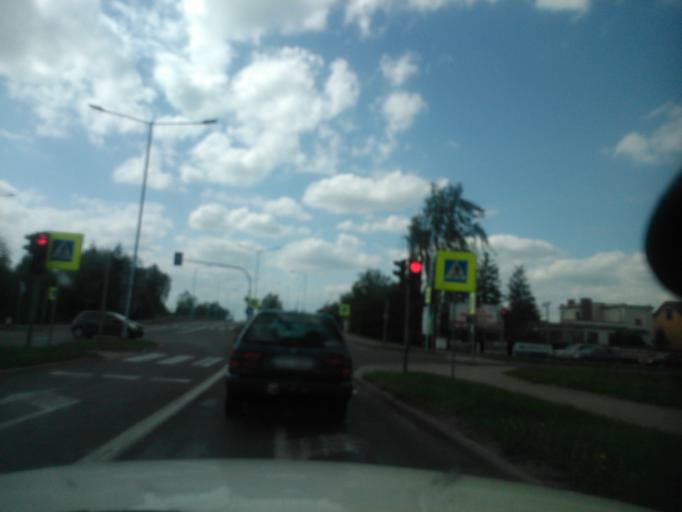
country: PL
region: Swietokrzyskie
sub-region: Powiat ostrowiecki
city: Ostrowiec Swietokrzyski
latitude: 50.9388
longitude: 21.3665
